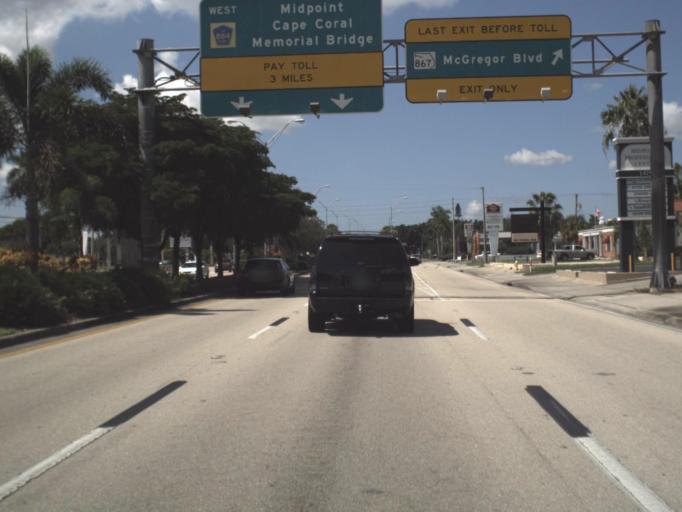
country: US
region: Florida
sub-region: Lee County
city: Whiskey Creek
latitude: 26.5968
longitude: -81.8861
